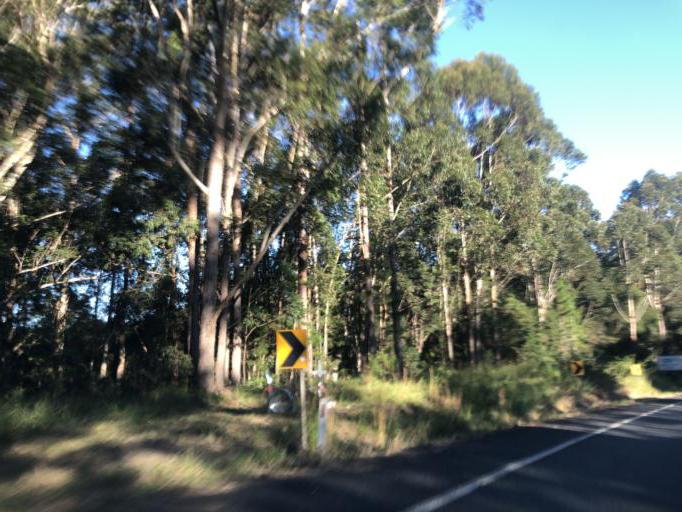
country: AU
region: New South Wales
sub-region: Nambucca Shire
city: Nambucca
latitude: -30.5506
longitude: 153.0087
